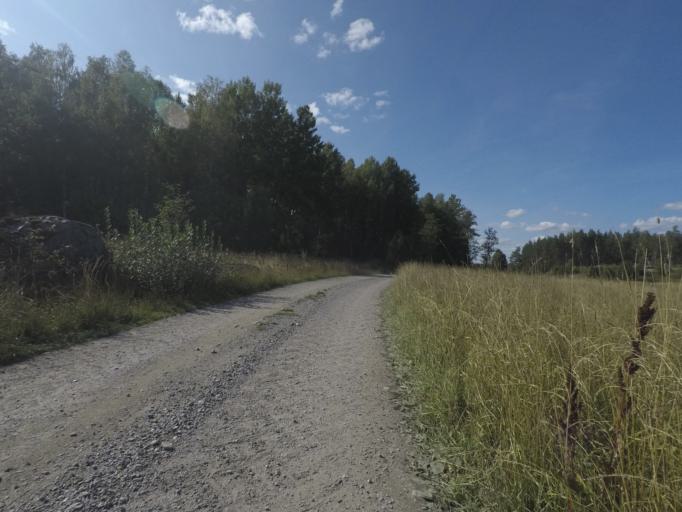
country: SE
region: Soedermanland
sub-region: Eskilstuna Kommun
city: Kvicksund
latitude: 59.4335
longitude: 16.2816
